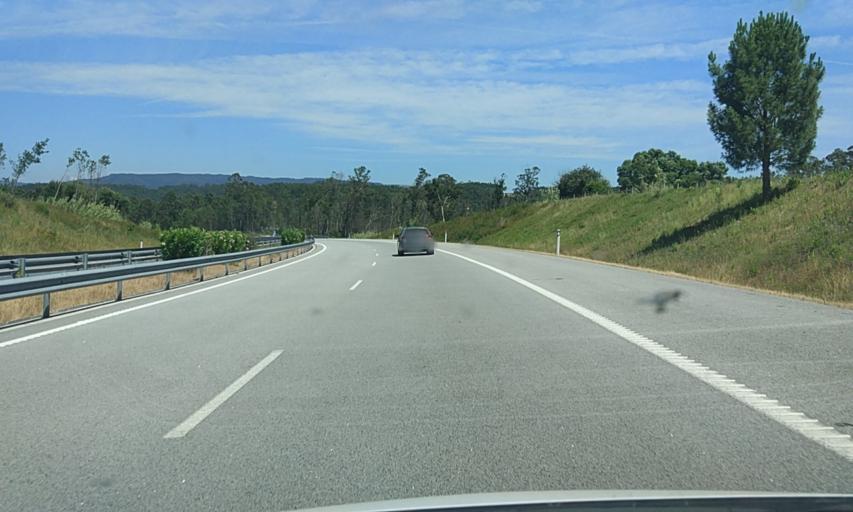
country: PT
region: Aveiro
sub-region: Mealhada
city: Pampilhosa do Botao
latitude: 40.2719
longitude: -8.5001
